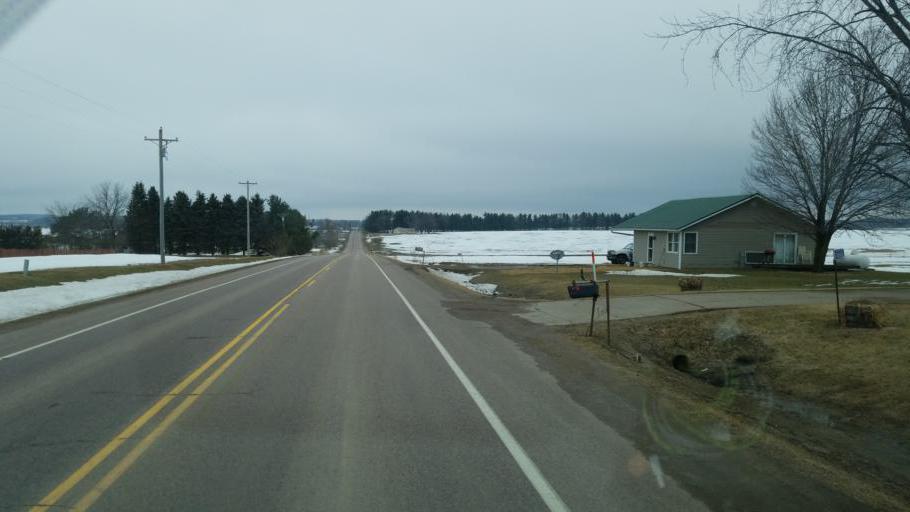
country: US
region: Wisconsin
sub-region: Wood County
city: Marshfield
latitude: 44.6431
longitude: -90.2184
